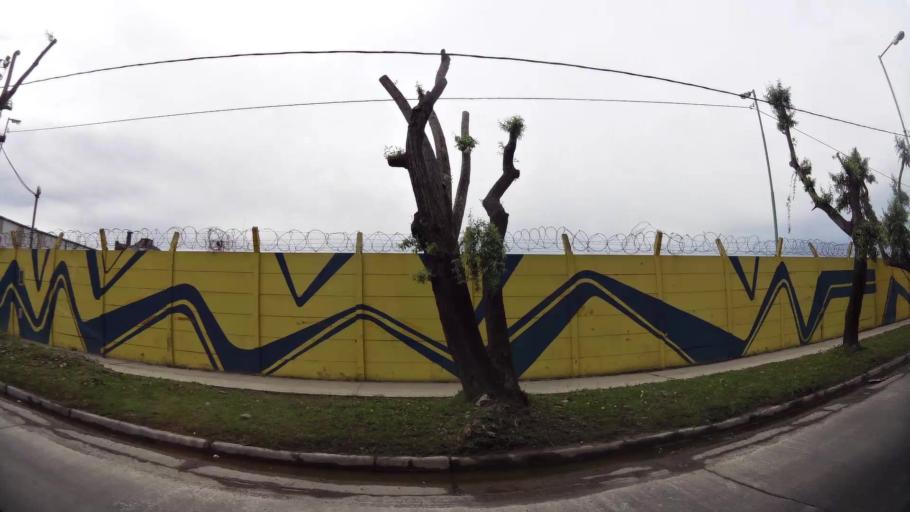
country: AR
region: Buenos Aires
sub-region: Partido de Avellaneda
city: Avellaneda
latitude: -34.6588
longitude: -58.3438
